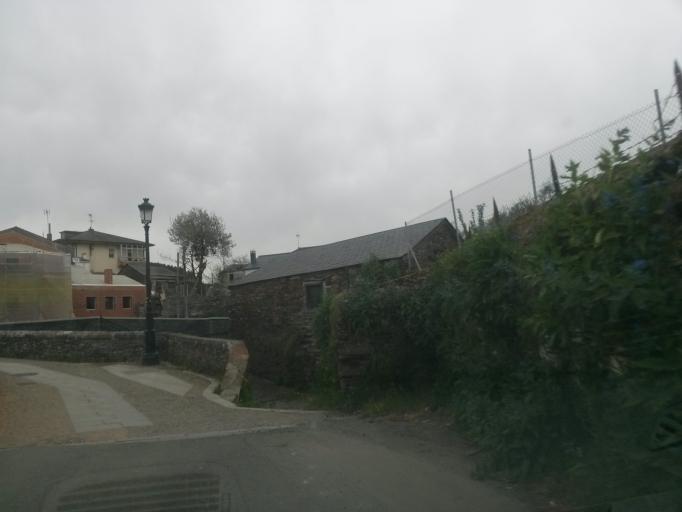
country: ES
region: Galicia
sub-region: Provincia de Lugo
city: Lugo
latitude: 43.0135
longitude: -7.5461
